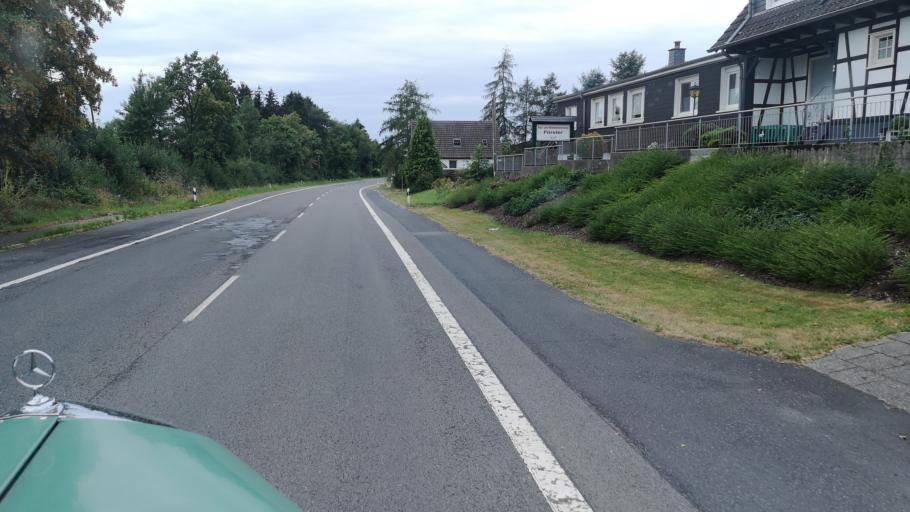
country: DE
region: North Rhine-Westphalia
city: Huckeswagen
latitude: 51.0924
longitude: 7.3157
